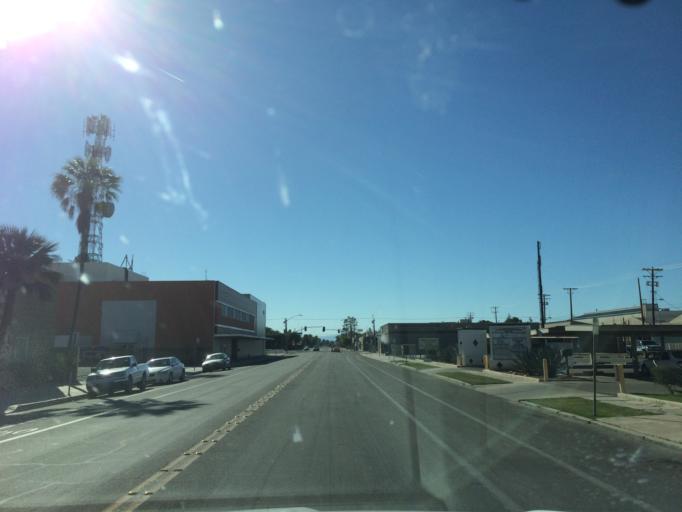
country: US
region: California
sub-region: Imperial County
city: El Centro
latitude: 32.7918
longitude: -115.5594
